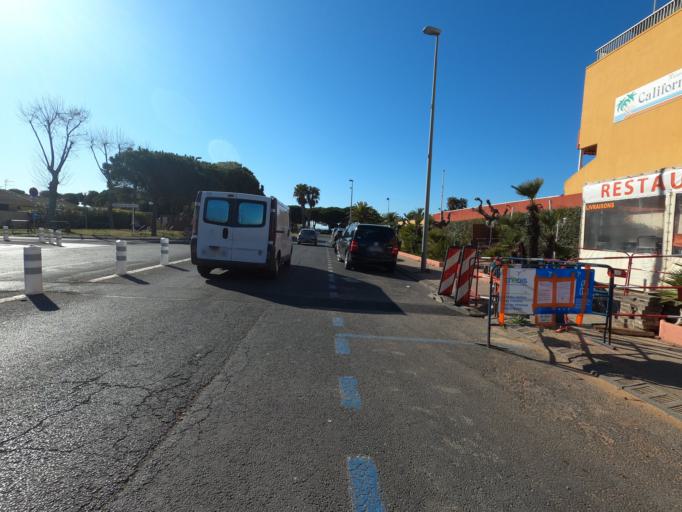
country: FR
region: Languedoc-Roussillon
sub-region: Departement de l'Herault
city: Palavas-les-Flots
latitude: 43.5295
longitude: 3.9244
